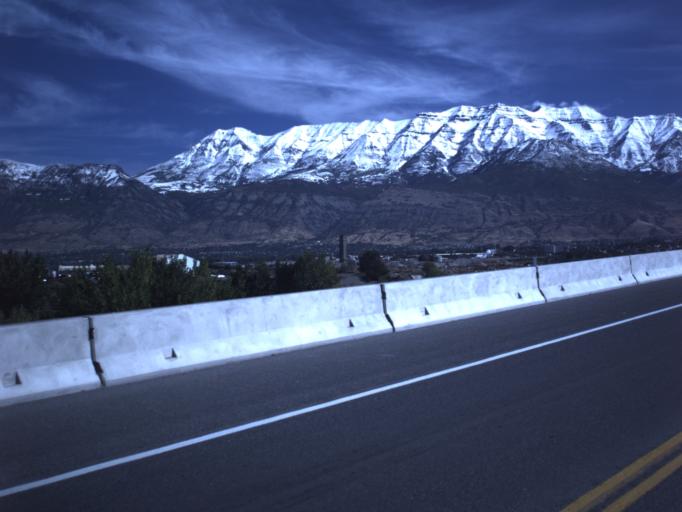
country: US
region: Utah
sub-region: Utah County
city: Lindon
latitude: 40.3104
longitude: -111.7503
